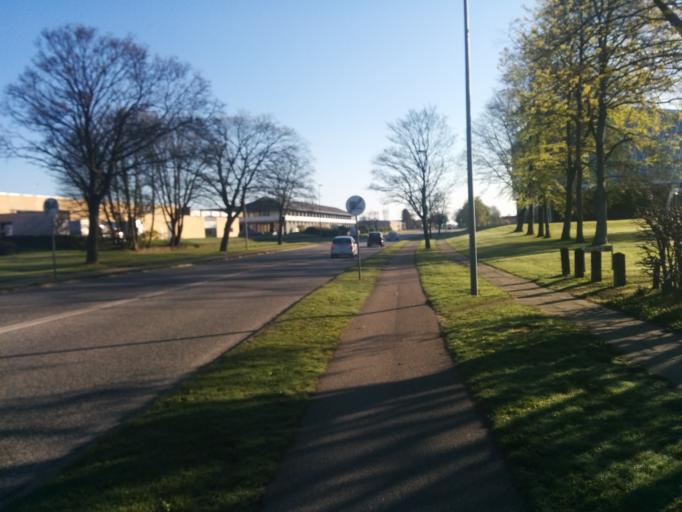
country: DK
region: Central Jutland
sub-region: Viborg Kommune
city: Viborg
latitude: 56.4579
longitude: 9.3959
